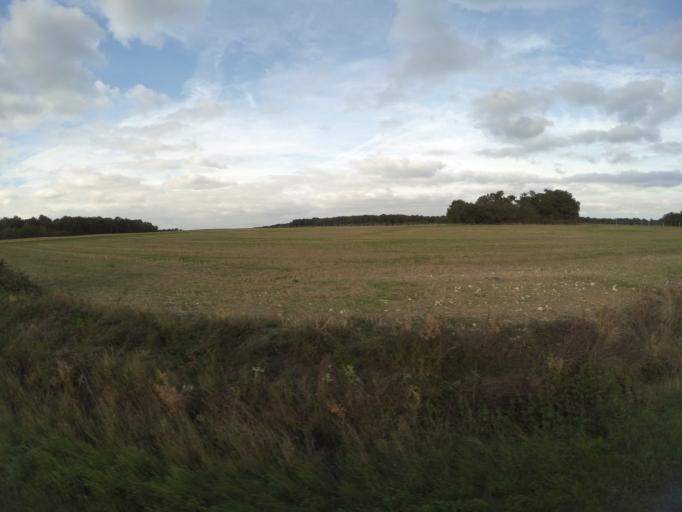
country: FR
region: Centre
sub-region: Departement d'Indre-et-Loire
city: Nazelles-Negron
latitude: 47.4554
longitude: 0.9391
